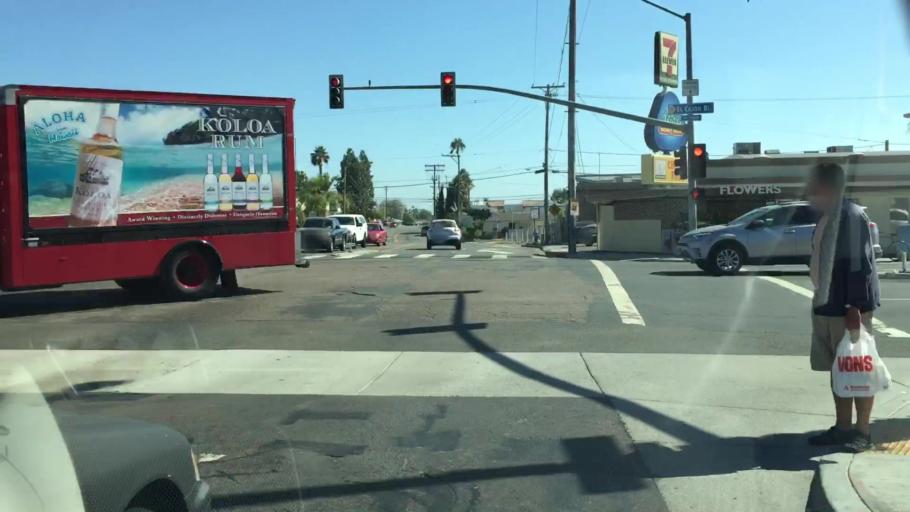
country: US
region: California
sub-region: San Diego County
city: La Mesa
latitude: 32.7689
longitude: -117.0472
